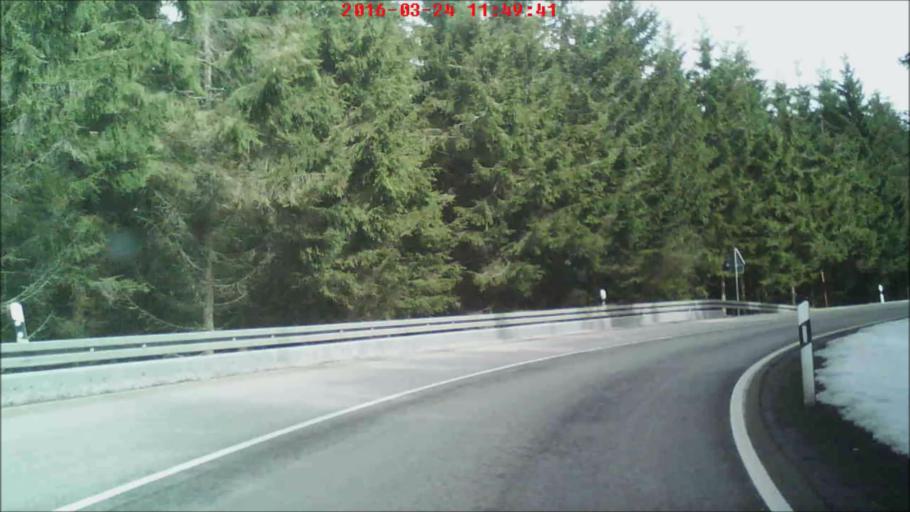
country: DE
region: Thuringia
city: Steinheid
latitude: 50.4629
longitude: 11.0361
